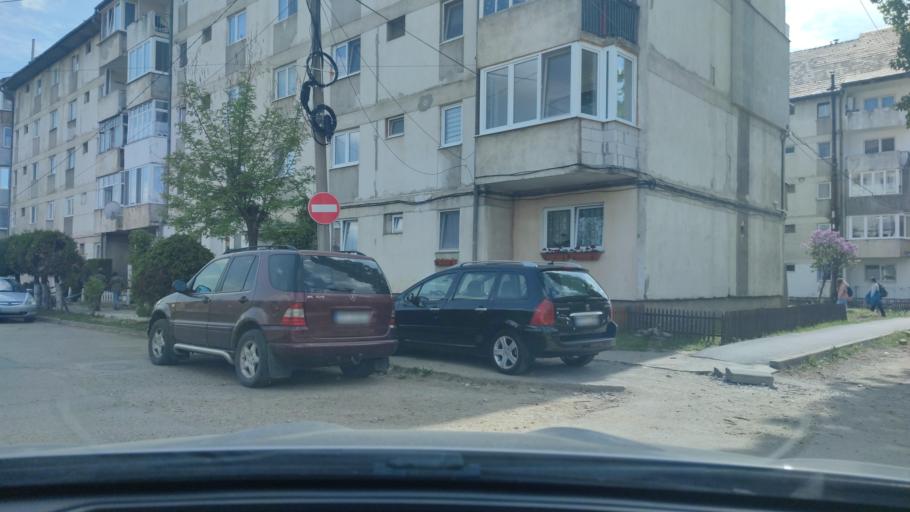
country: RO
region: Harghita
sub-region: Municipiul Gheorgheni
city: Gheorgheni
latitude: 46.7197
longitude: 25.5898
